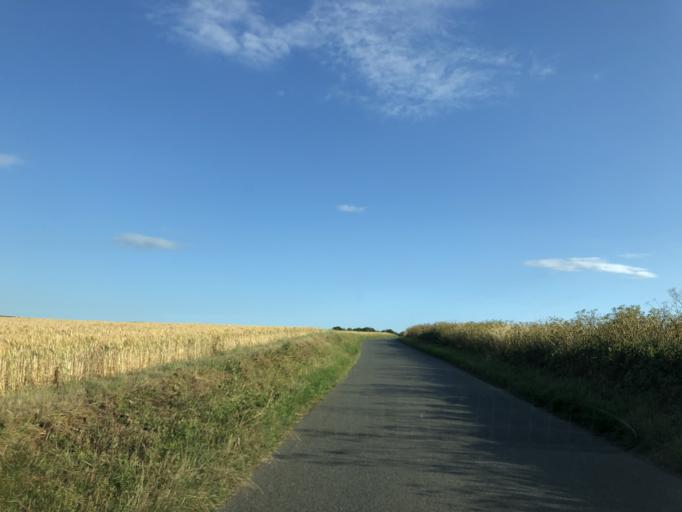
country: GB
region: England
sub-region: Isle of Wight
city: Yarmouth
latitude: 50.6931
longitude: -1.4725
